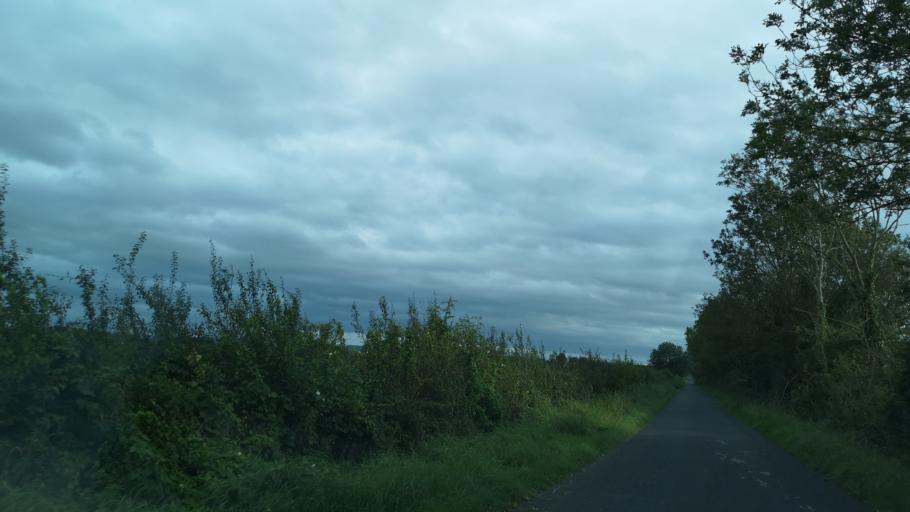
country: IE
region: Leinster
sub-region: Uibh Fhaili
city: Ferbane
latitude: 53.1913
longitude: -7.7263
